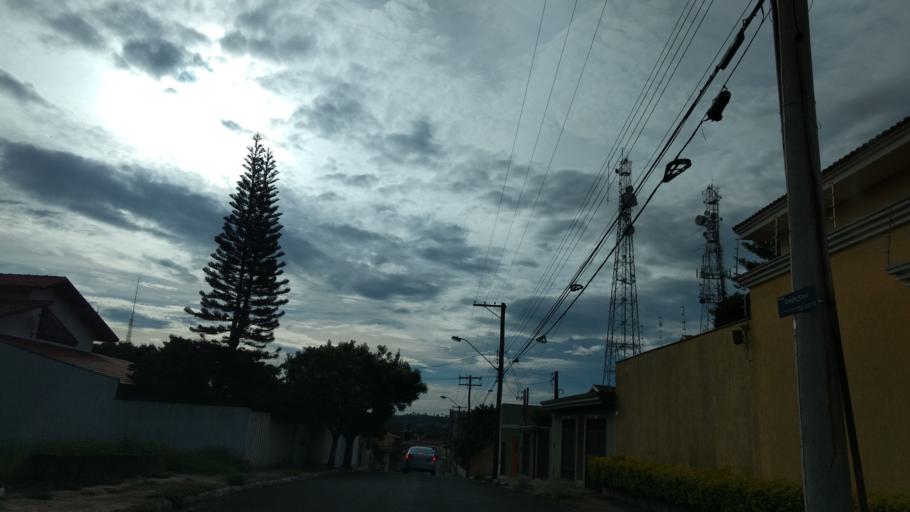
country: BR
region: Sao Paulo
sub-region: Botucatu
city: Botucatu
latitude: -22.9005
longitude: -48.4459
